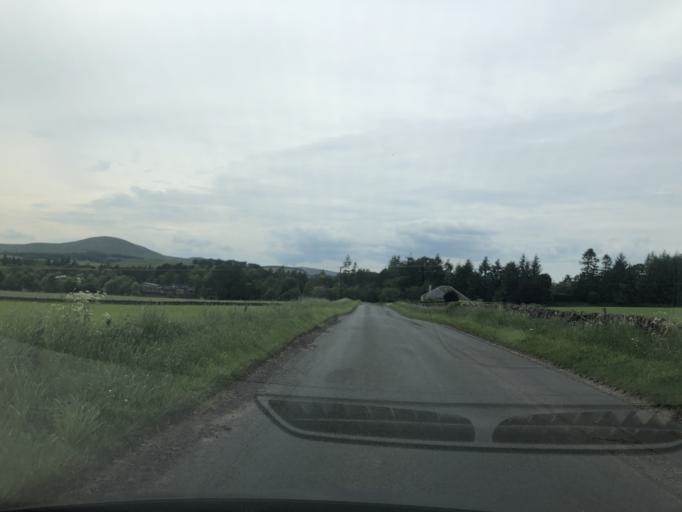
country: GB
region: Scotland
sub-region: The Scottish Borders
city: West Linton
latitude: 55.7407
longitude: -3.3369
